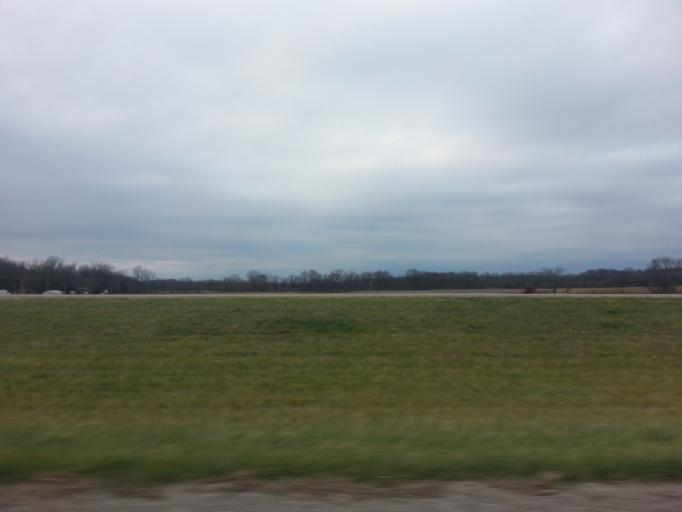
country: US
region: Iowa
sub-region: Henry County
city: Mount Pleasant
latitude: 40.8993
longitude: -91.5537
